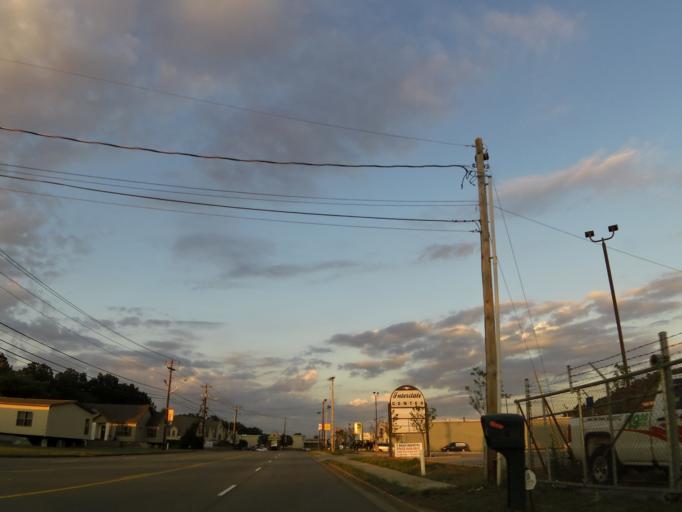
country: US
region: Tennessee
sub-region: Putnam County
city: Cookeville
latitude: 36.1385
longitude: -85.5207
